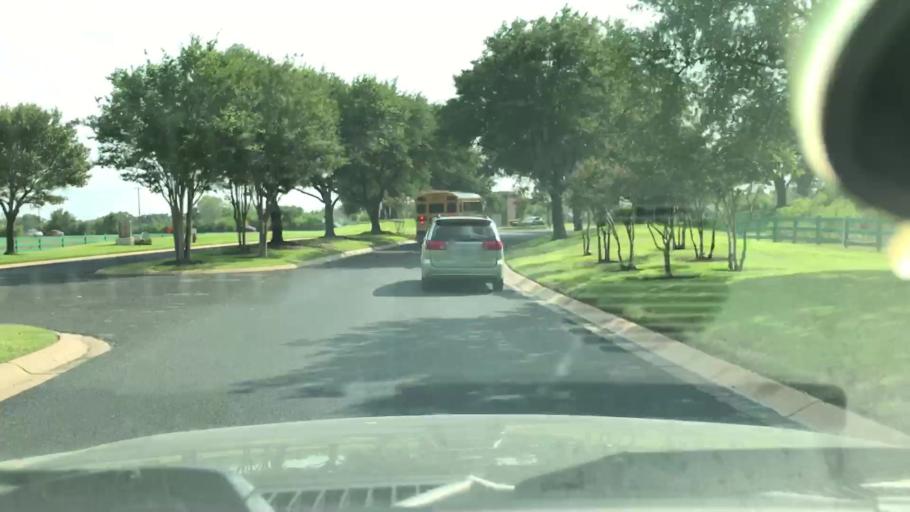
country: US
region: Texas
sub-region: Williamson County
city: Leander
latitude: 30.5437
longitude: -97.8383
